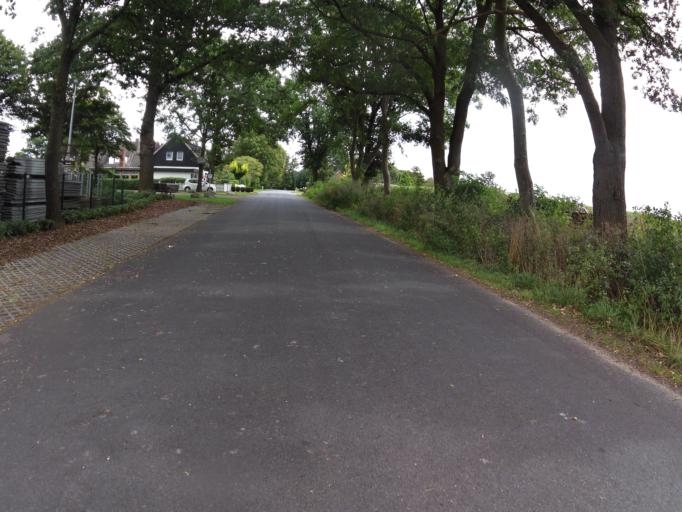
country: DE
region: Lower Saxony
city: Lunestedt
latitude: 53.4930
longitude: 8.7201
